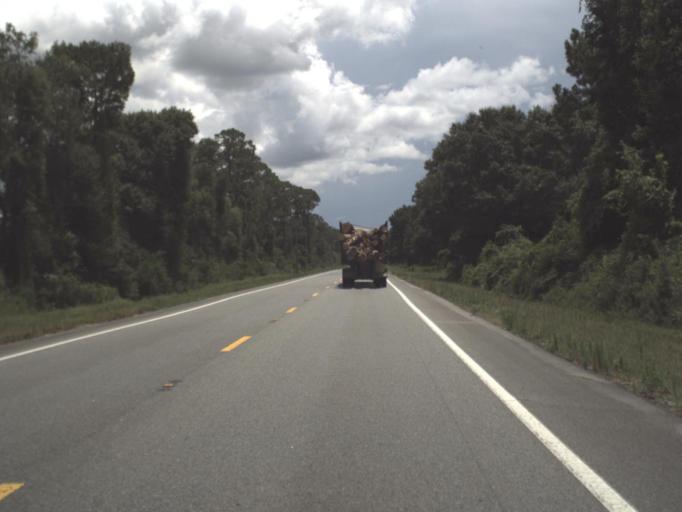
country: US
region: Florida
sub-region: Taylor County
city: Perry
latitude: 30.0997
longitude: -83.6948
